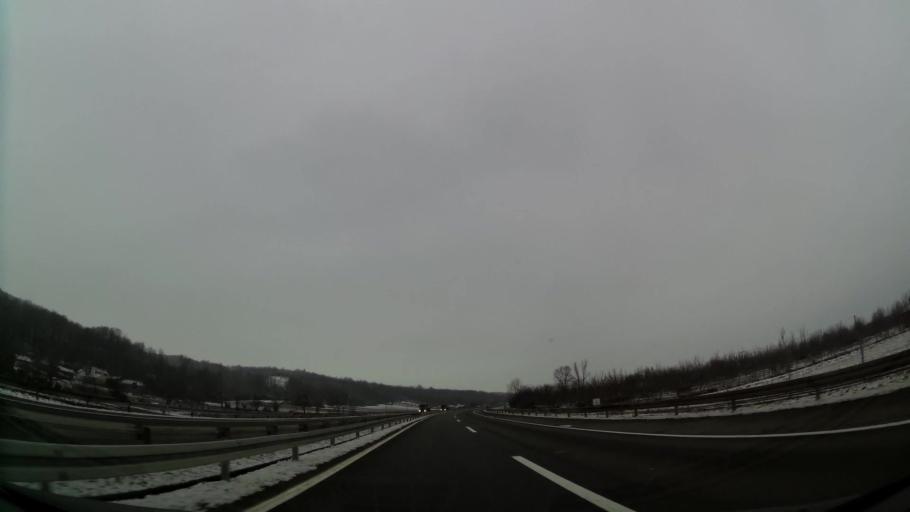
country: RS
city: Lugavcina
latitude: 44.4321
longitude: 21.0531
